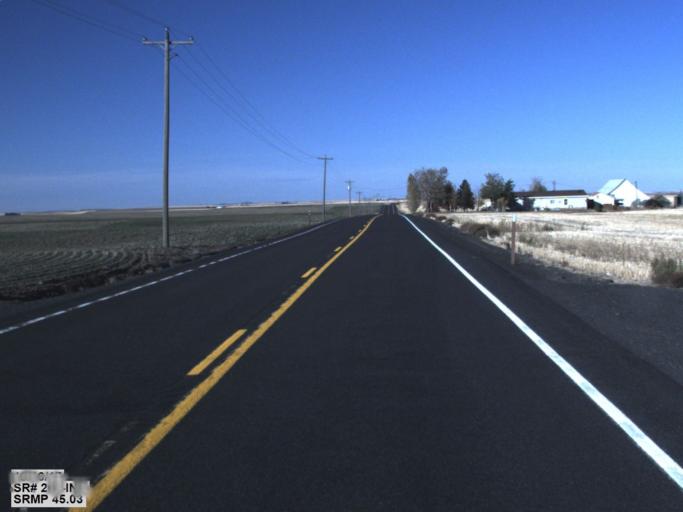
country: US
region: Washington
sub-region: Adams County
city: Ritzville
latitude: 46.8716
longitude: -118.3356
